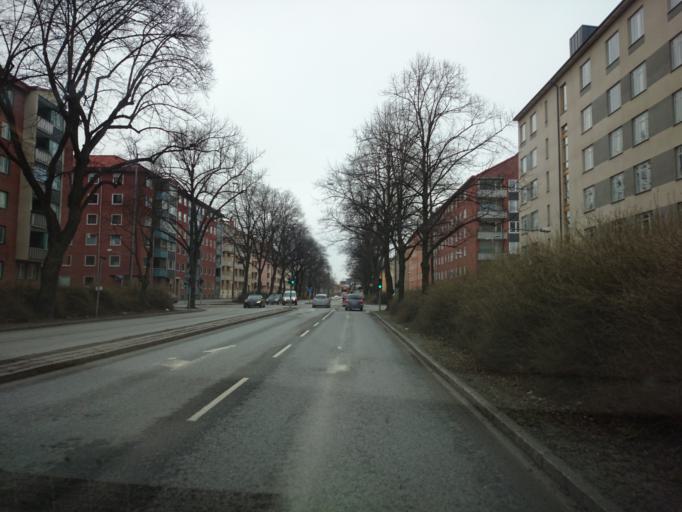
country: SE
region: Uppsala
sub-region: Uppsala Kommun
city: Uppsala
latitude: 59.8626
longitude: 17.6233
